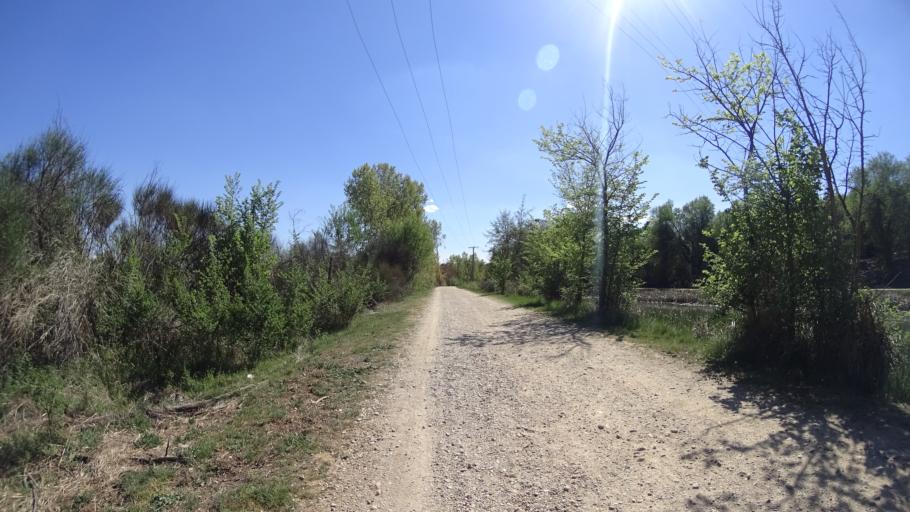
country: ES
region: Castille and Leon
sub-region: Provincia de Valladolid
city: Santovenia de Pisuerga
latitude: 41.6920
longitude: -4.7158
